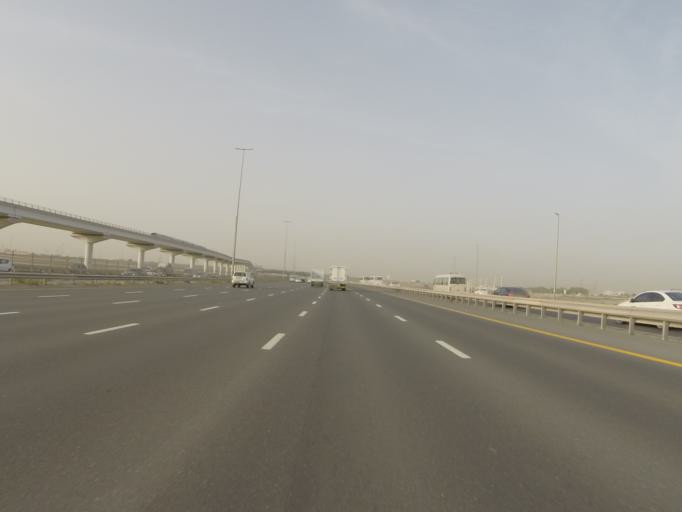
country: AE
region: Dubai
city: Dubai
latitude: 25.0224
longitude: 55.0983
